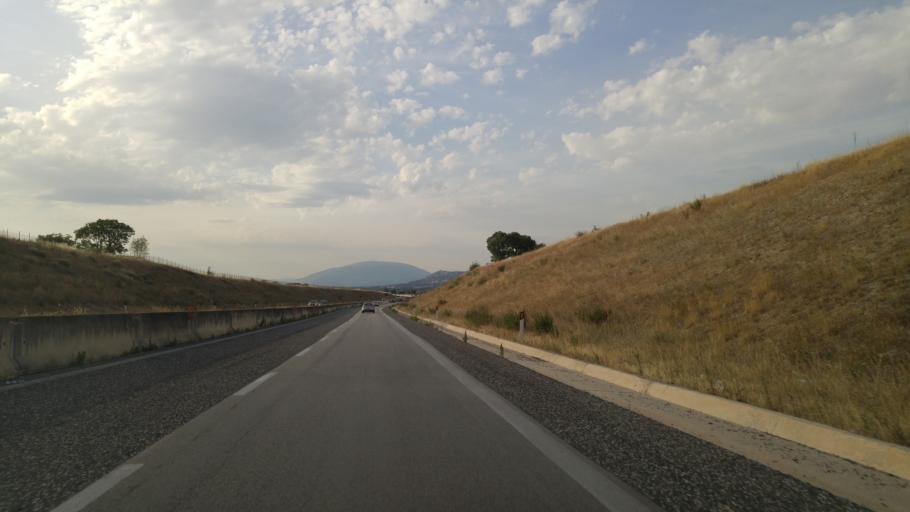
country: IT
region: Umbria
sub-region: Provincia di Perugia
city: San Giacomo
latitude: 42.8008
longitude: 12.7613
